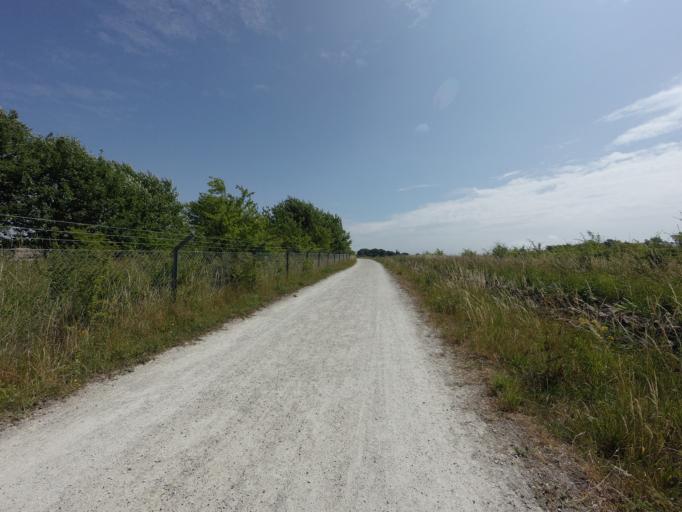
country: SE
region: Skane
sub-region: Malmo
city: Bunkeflostrand
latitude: 55.5643
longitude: 12.9321
